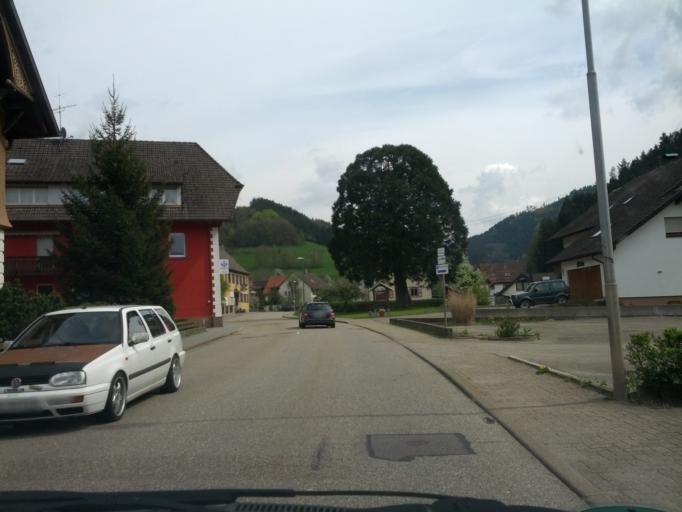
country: DE
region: Baden-Wuerttemberg
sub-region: Freiburg Region
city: Elzach
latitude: 48.0990
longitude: 8.0585
